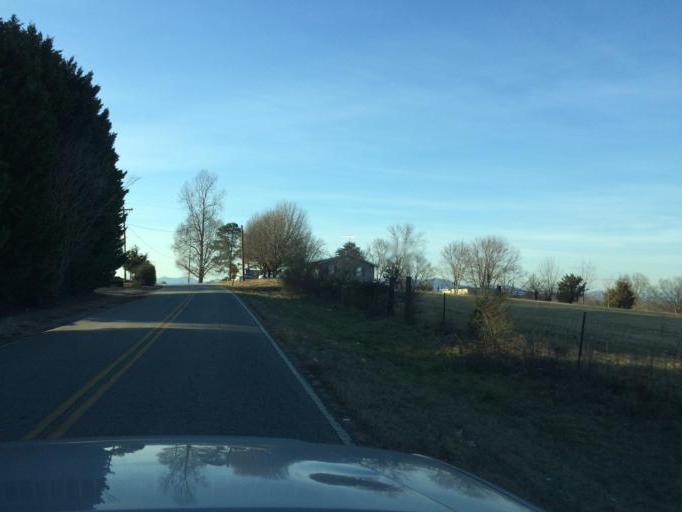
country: US
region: South Carolina
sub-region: Spartanburg County
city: Landrum
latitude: 35.1472
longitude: -82.1065
